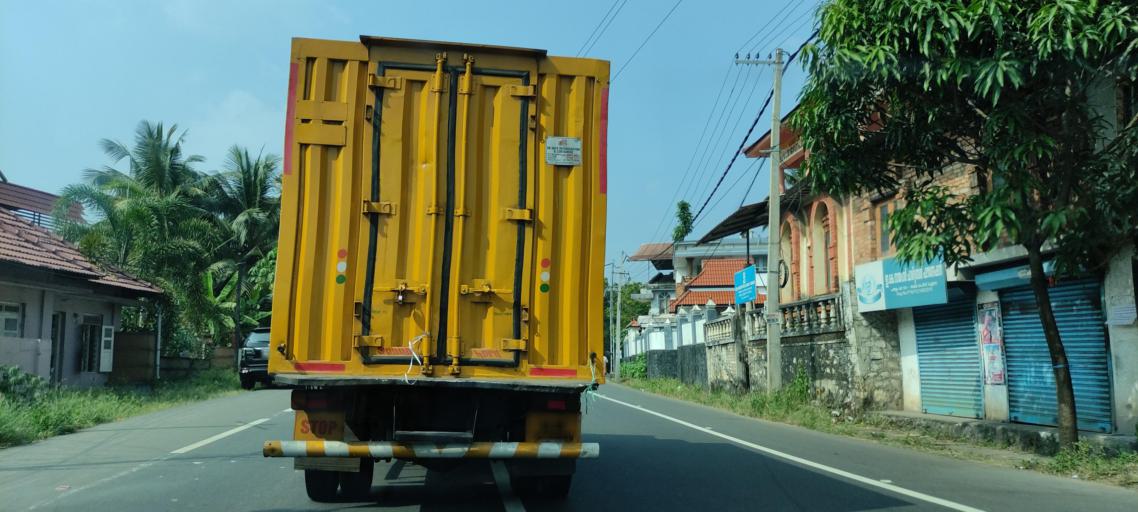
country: IN
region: Kerala
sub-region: Pattanamtitta
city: Adur
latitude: 9.2375
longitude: 76.6720
